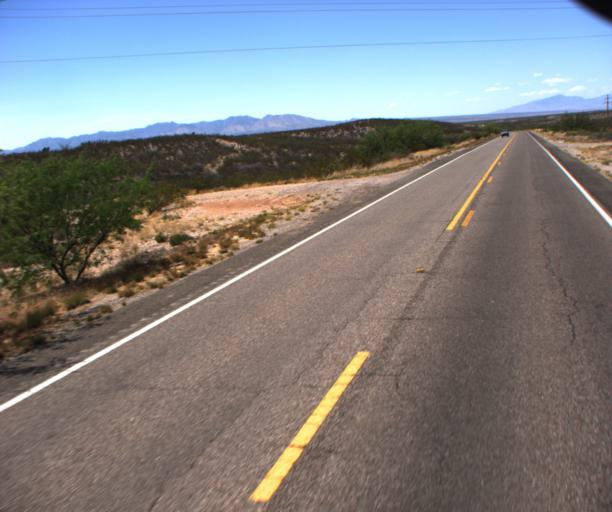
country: US
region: Arizona
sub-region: Cochise County
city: Tombstone
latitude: 31.7738
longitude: -110.1285
